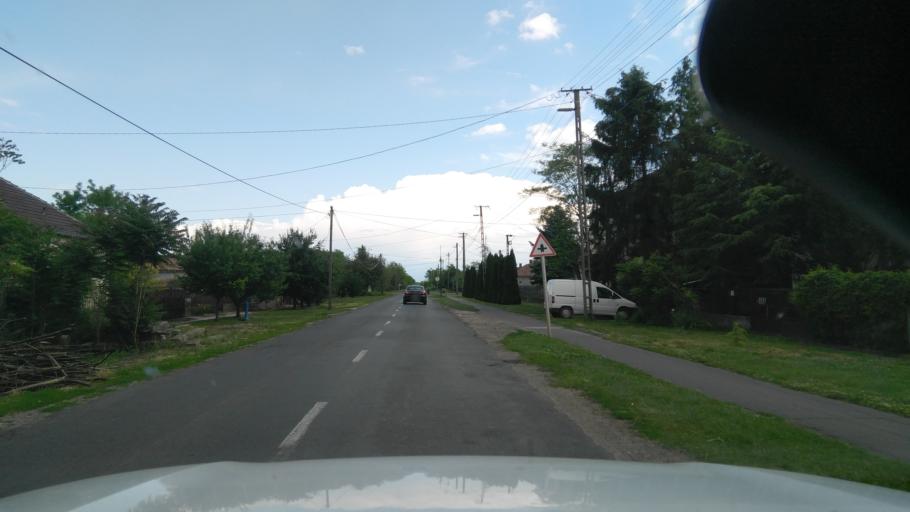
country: HU
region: Bekes
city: Magyarbanhegyes
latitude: 46.4511
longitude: 20.9736
